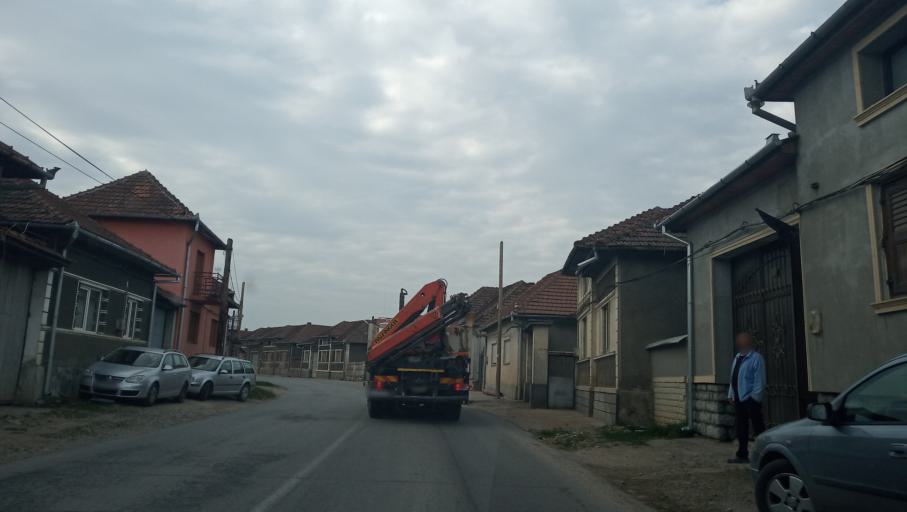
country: RO
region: Bihor
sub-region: Comuna Lunca
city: Lunca
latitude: 46.5201
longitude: 22.4638
